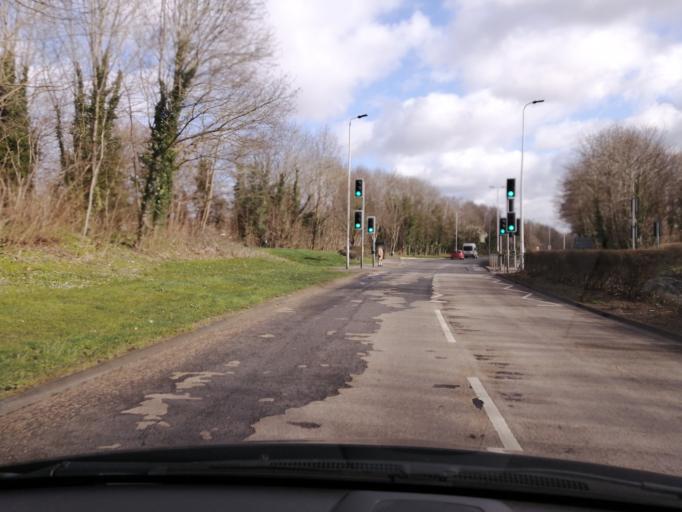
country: GB
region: England
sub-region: Peterborough
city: Marholm
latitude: 52.6038
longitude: -0.2868
